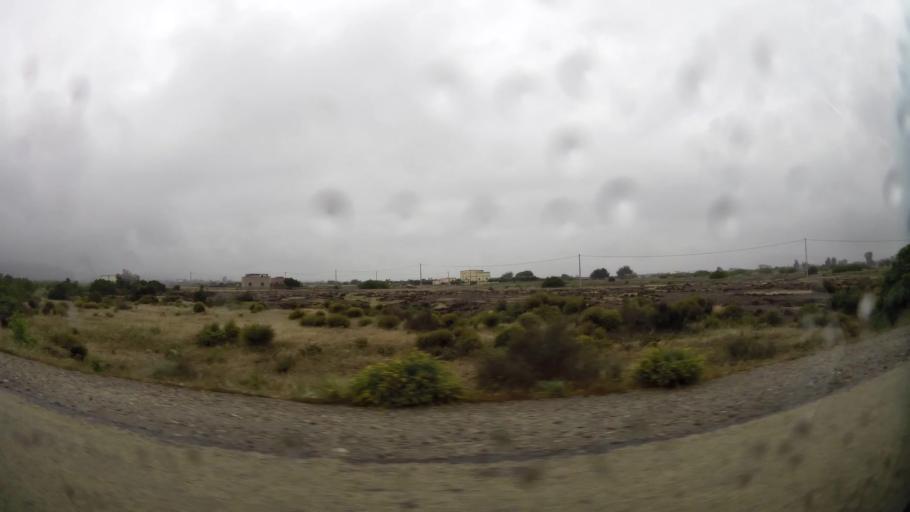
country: MA
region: Taza-Al Hoceima-Taounate
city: Imzourene
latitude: 35.1405
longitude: -3.7905
